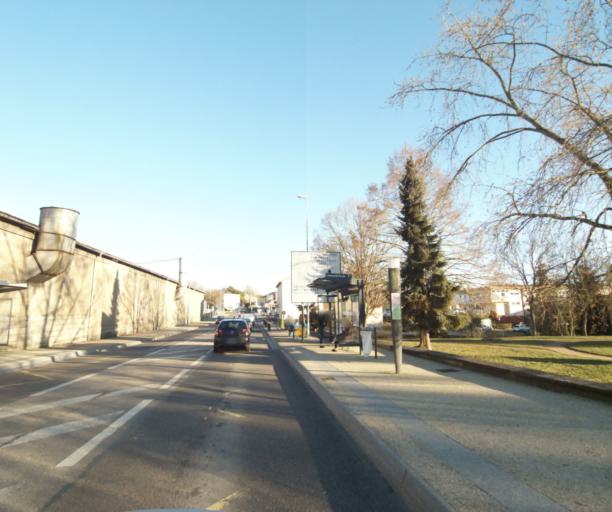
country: FR
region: Lorraine
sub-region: Departement de Meurthe-et-Moselle
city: Laneuveville-devant-Nancy
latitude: 48.6592
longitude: 6.2276
